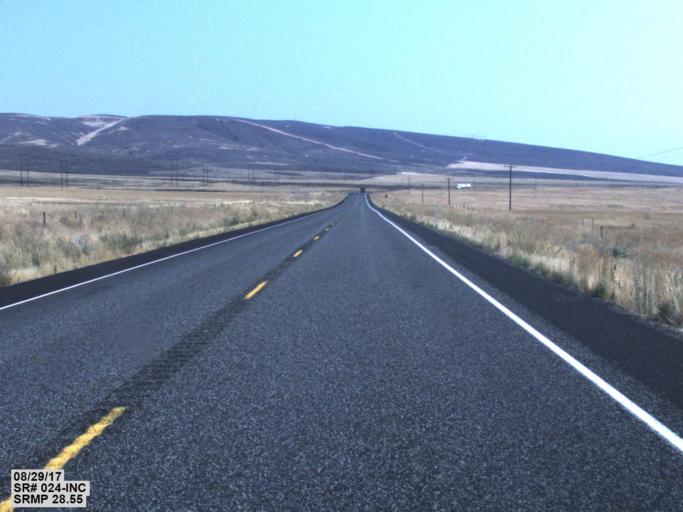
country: US
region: Washington
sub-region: Grant County
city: Desert Aire
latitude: 46.5338
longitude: -119.9201
